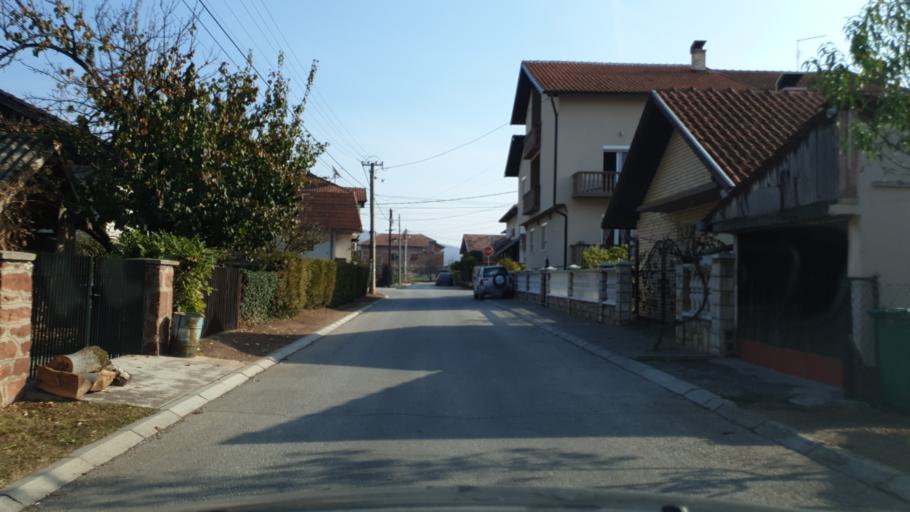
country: RS
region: Central Serbia
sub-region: Pomoravski Okrug
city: Paracin
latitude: 43.8573
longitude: 21.4253
